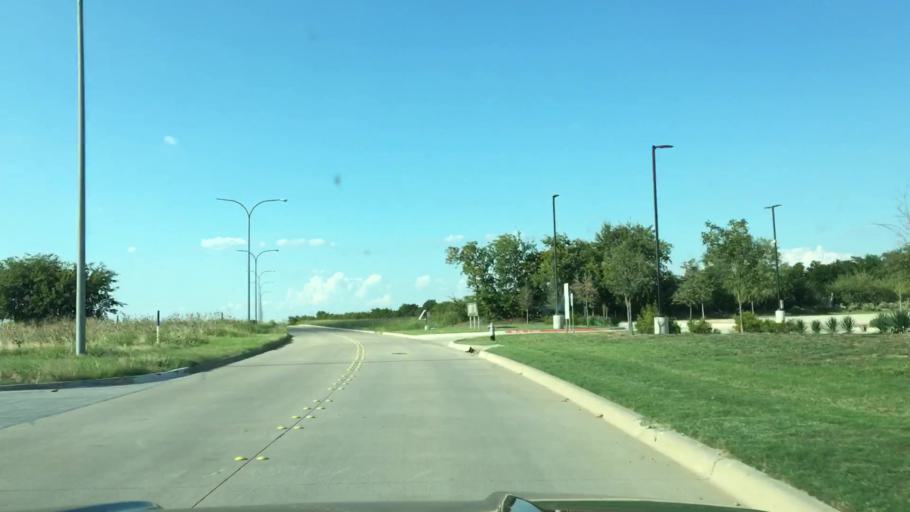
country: US
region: Texas
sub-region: Tarrant County
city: Haslet
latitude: 32.9996
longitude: -97.3588
